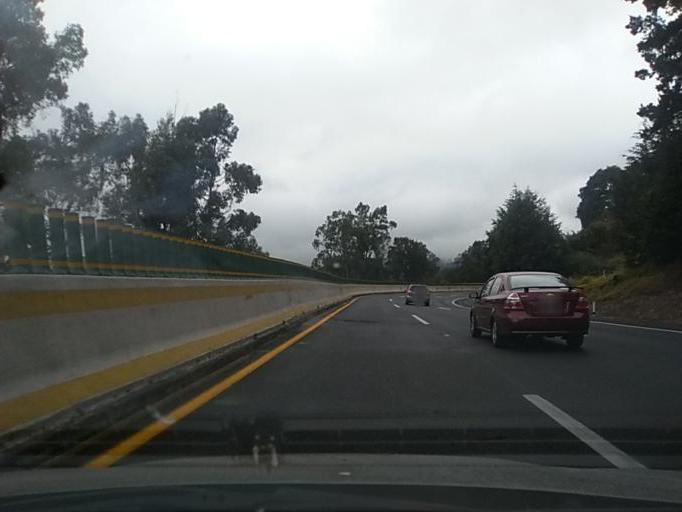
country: MX
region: Mexico City
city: Xochimilco
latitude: 19.2103
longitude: -99.1344
